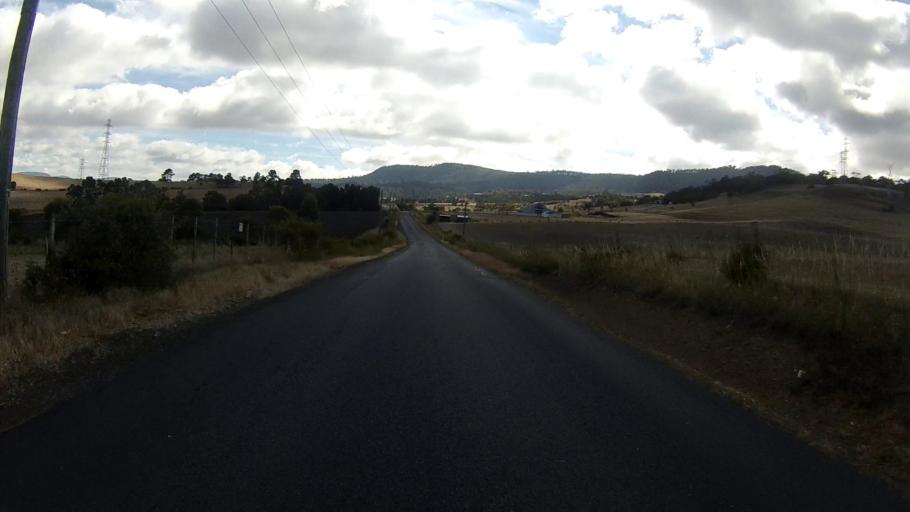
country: AU
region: Tasmania
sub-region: Brighton
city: Old Beach
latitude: -42.7708
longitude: 147.2927
